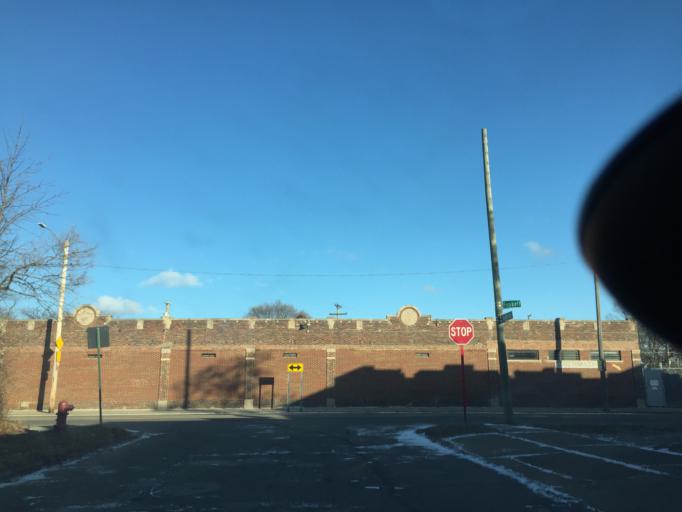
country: US
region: Michigan
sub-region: Wayne County
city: Highland Park
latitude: 42.4000
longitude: -83.1303
